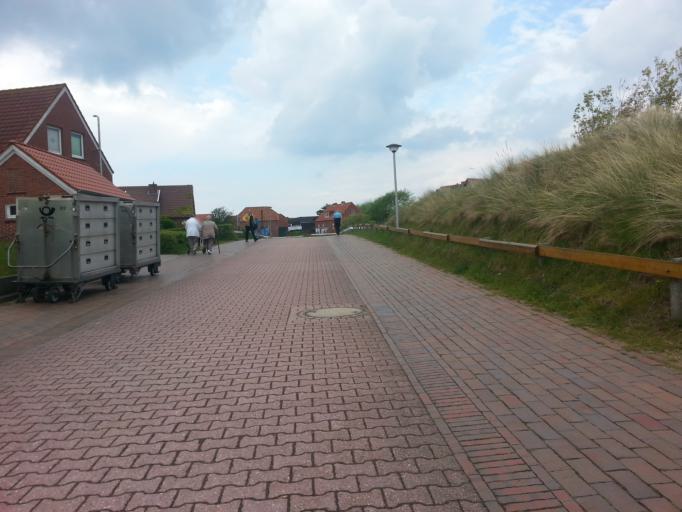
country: DE
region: Lower Saxony
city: Baltrum
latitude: 53.7267
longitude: 7.3678
